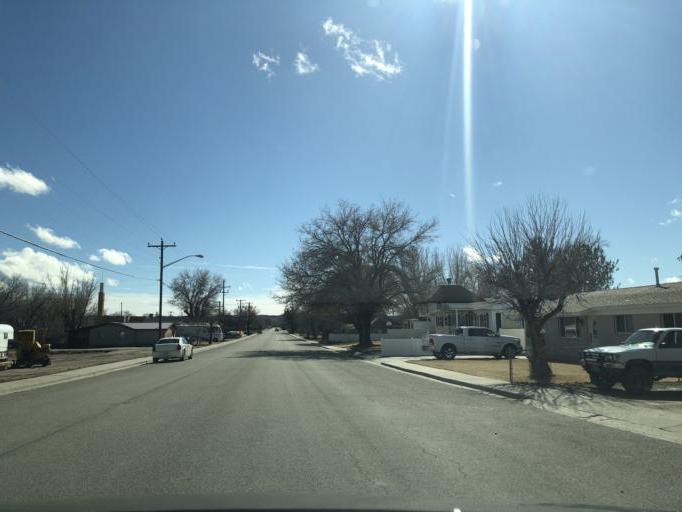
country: US
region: Utah
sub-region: Carbon County
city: East Carbon City
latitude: 38.9988
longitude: -110.1622
